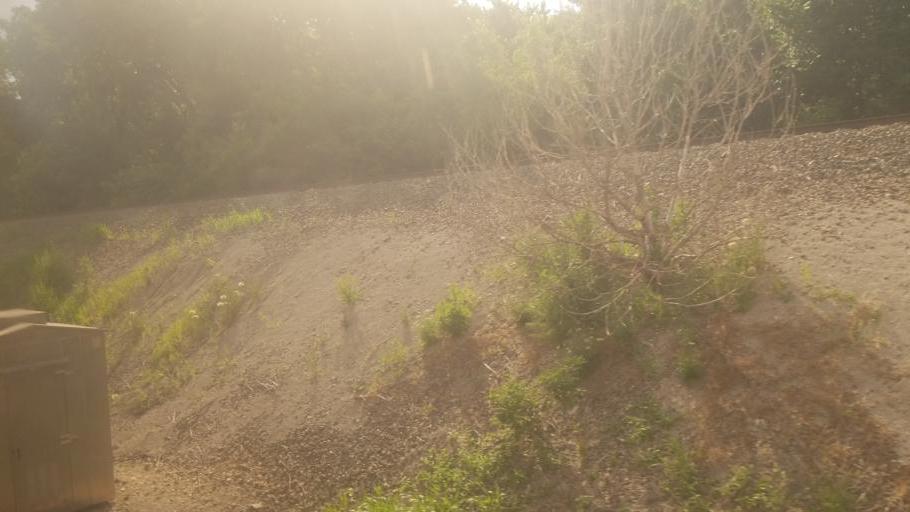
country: US
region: Kansas
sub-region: Johnson County
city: Shawnee
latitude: 39.0748
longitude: -94.7304
